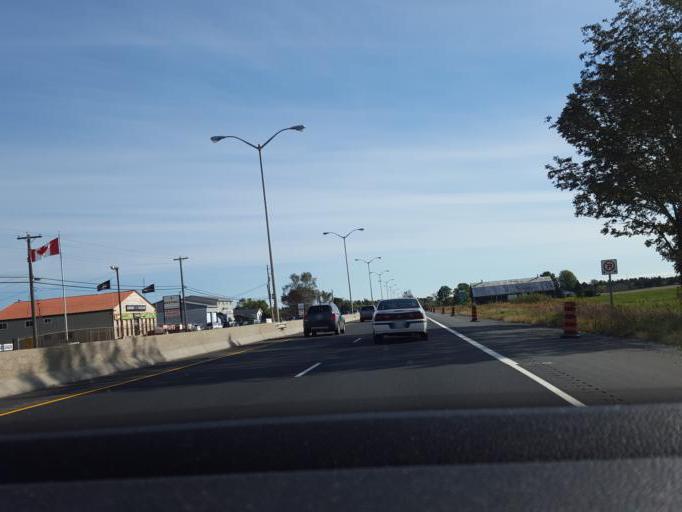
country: CA
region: Ontario
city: Oshawa
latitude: 43.9558
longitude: -78.6080
